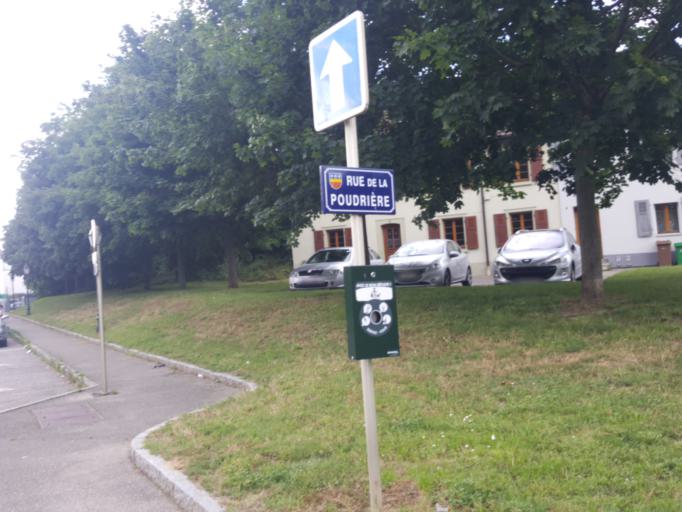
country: FR
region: Alsace
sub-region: Departement du Haut-Rhin
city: Huningue
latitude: 47.5936
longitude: 7.5843
